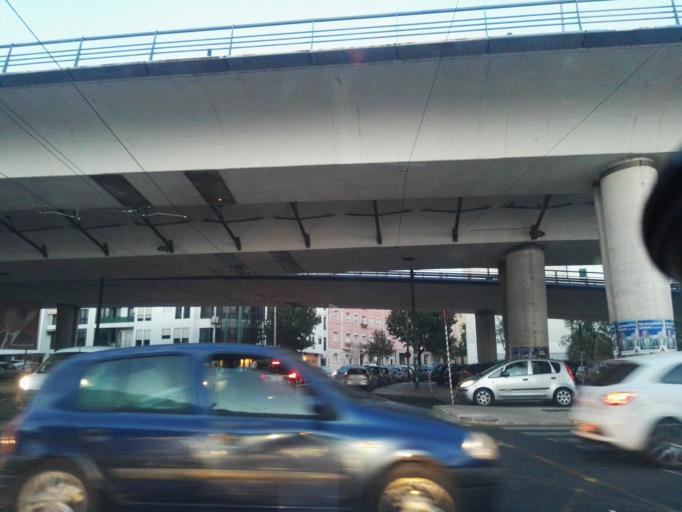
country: PT
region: Lisbon
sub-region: Oeiras
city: Alges
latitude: 38.6998
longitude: -9.2275
